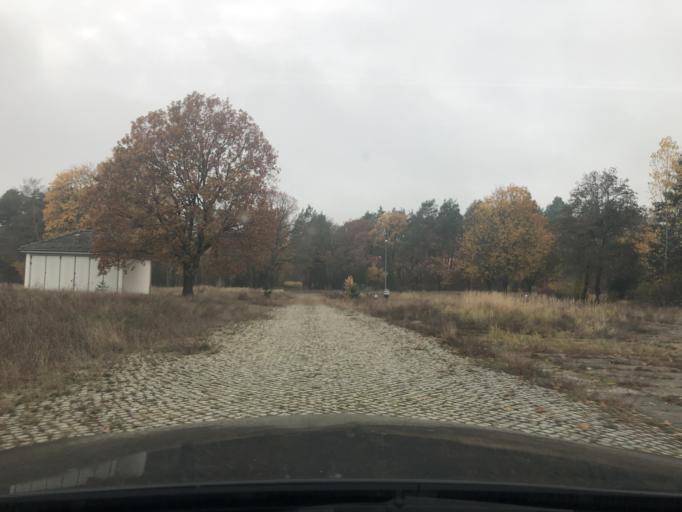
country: DE
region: Mecklenburg-Vorpommern
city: Eggesin
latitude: 53.6647
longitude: 14.1139
